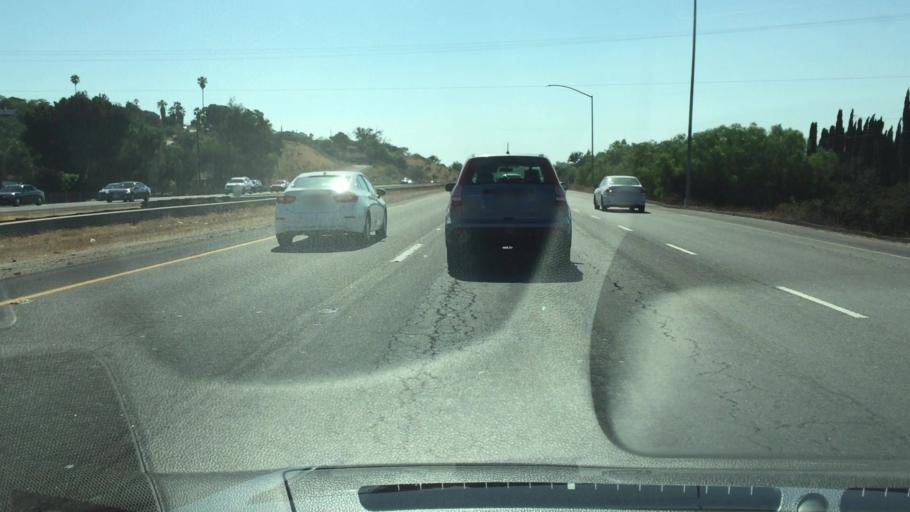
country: US
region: California
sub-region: San Diego County
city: Spring Valley
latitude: 32.7447
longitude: -116.9786
